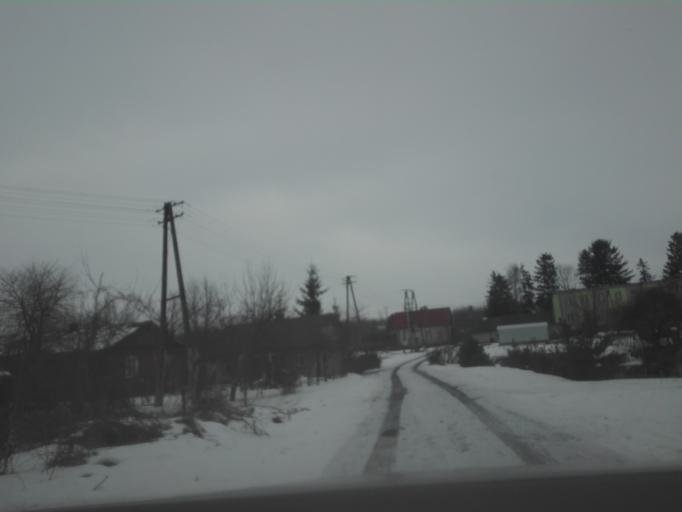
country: PL
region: Lublin Voivodeship
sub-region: Powiat hrubieszowski
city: Horodlo
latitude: 50.8424
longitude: 24.0294
